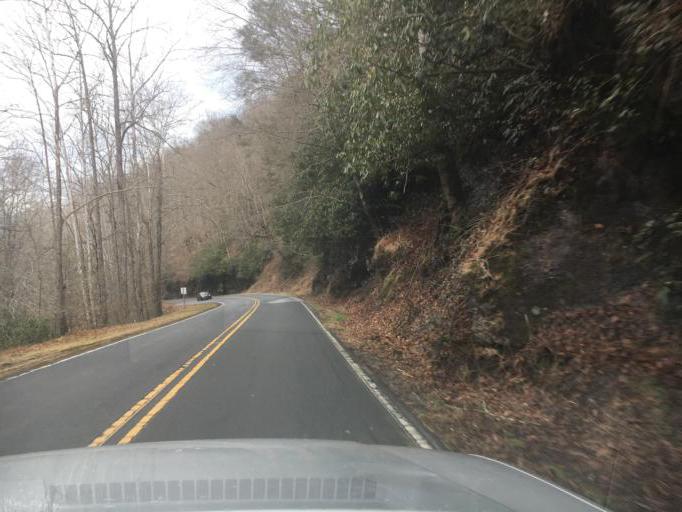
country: US
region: North Carolina
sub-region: Transylvania County
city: Brevard
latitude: 35.2827
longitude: -82.7583
